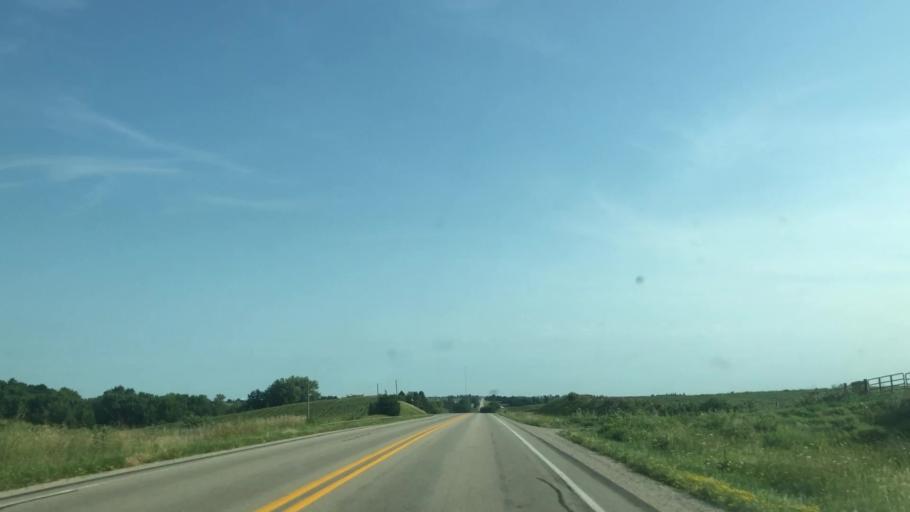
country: US
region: Iowa
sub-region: Marshall County
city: Marshalltown
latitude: 42.0428
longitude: -93.0002
